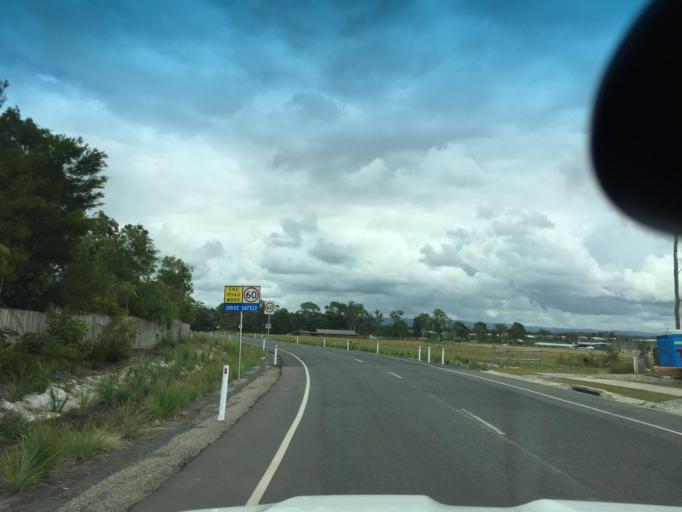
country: AU
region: Queensland
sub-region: Moreton Bay
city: Burpengary
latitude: -27.1649
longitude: 152.9840
